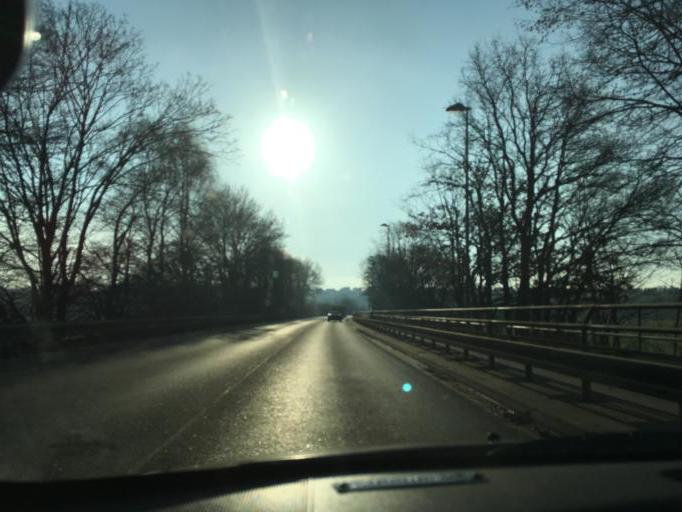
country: DE
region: North Rhine-Westphalia
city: Schwerte
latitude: 51.4404
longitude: 7.5788
